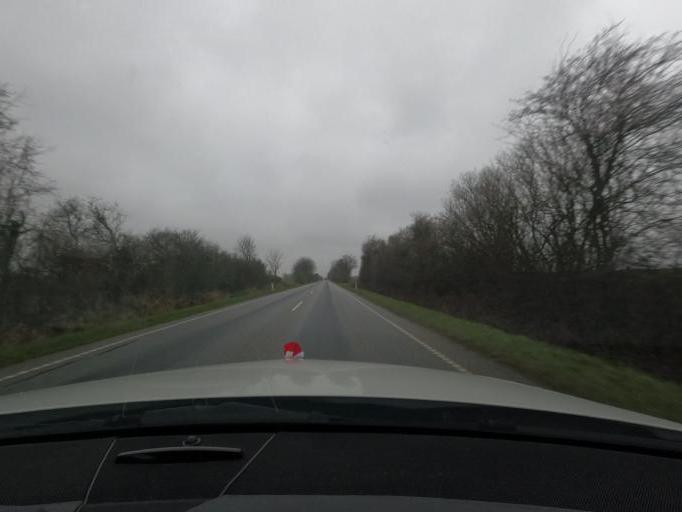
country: DK
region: South Denmark
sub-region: Haderslev Kommune
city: Starup
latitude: 55.2061
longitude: 9.5571
